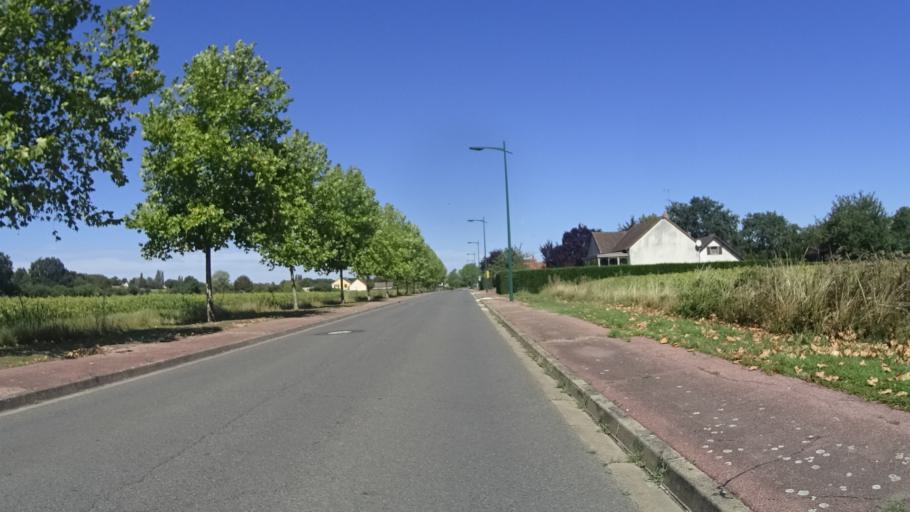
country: FR
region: Centre
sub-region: Departement du Cher
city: Belleville-sur-Loire
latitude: 47.5101
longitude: 2.8487
